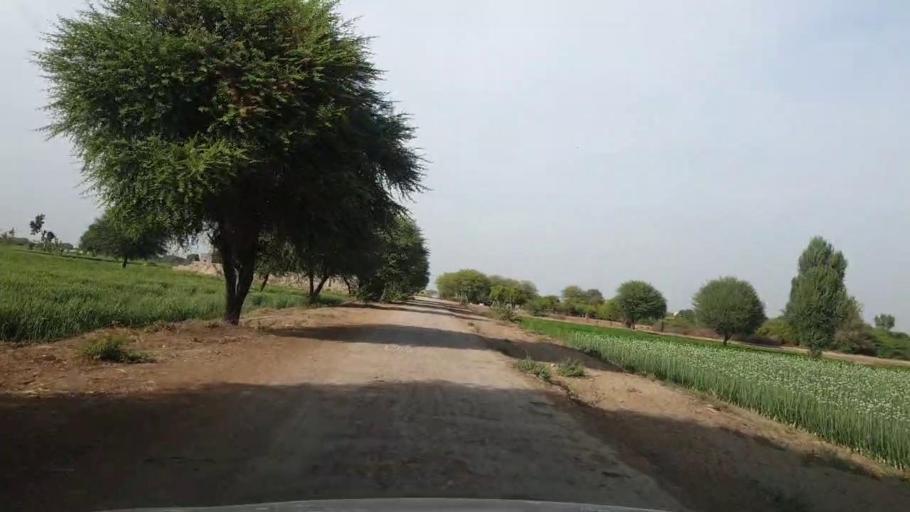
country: PK
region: Sindh
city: Kunri
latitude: 25.1383
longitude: 69.4605
